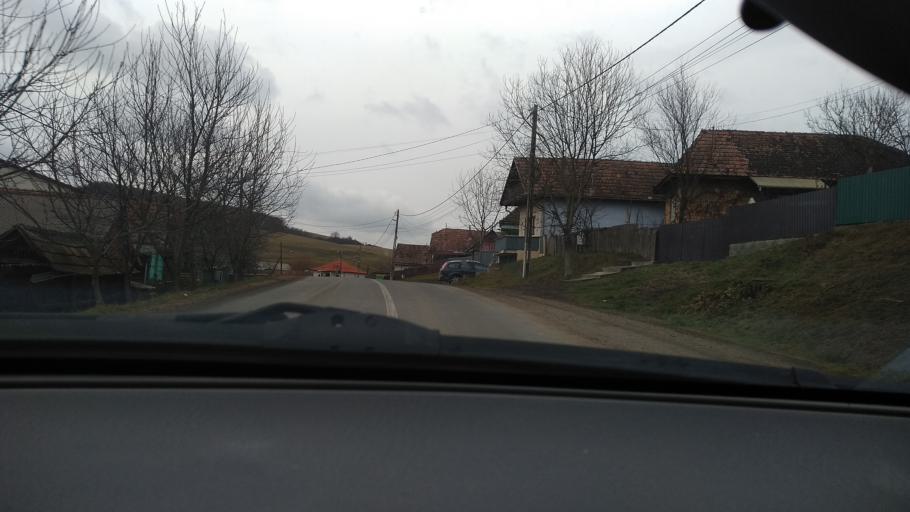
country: RO
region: Mures
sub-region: Comuna Galesti
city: Galesti
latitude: 46.5431
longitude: 24.7537
